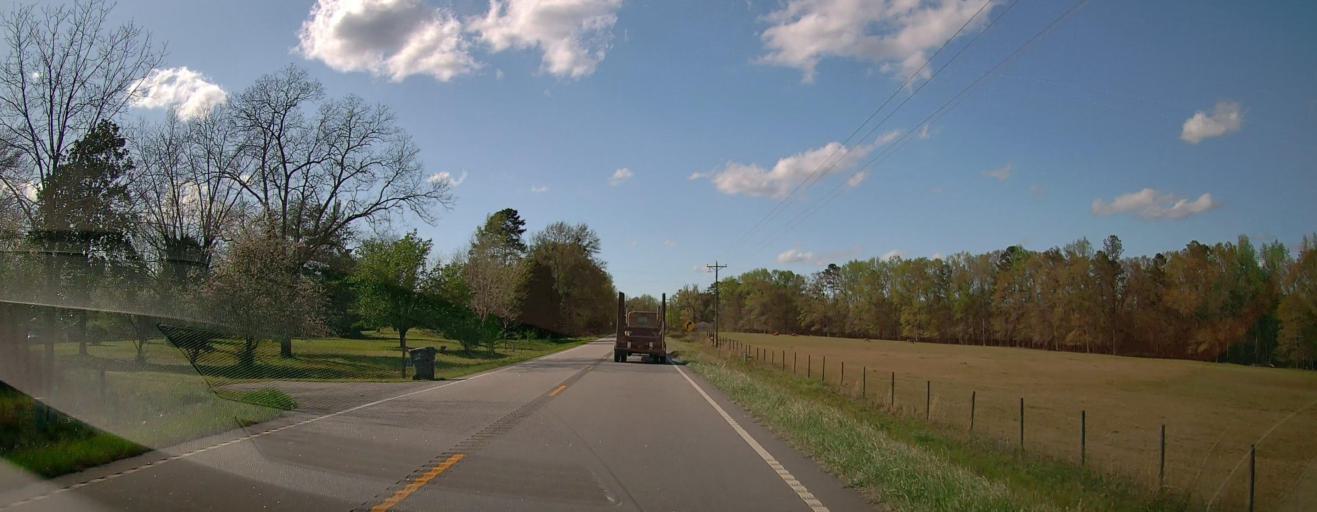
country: US
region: Georgia
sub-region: Baldwin County
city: Hardwick
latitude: 33.0572
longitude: -83.1267
